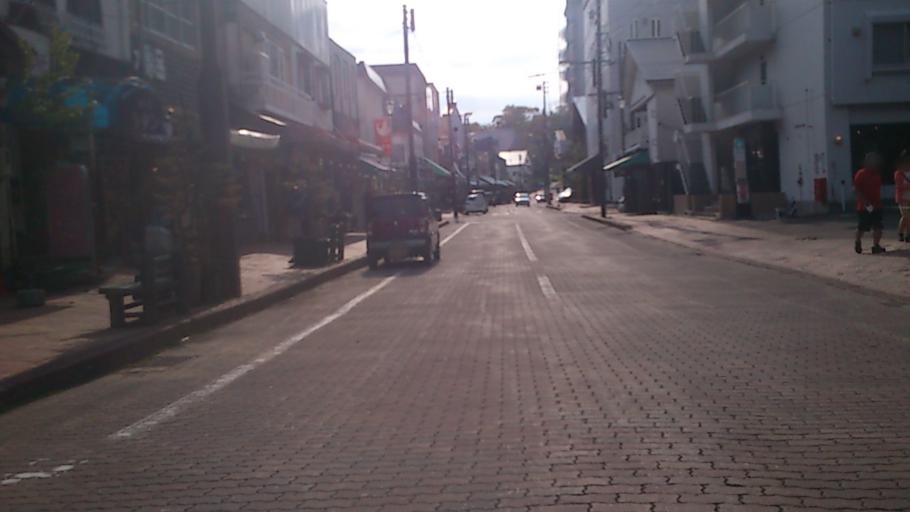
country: JP
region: Hokkaido
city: Bihoro
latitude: 43.4339
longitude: 144.0933
